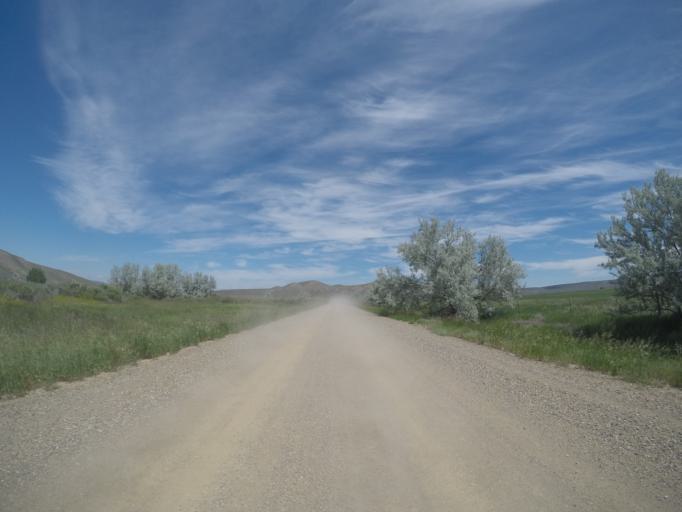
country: US
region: Montana
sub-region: Carbon County
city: Red Lodge
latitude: 45.2251
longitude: -108.8421
